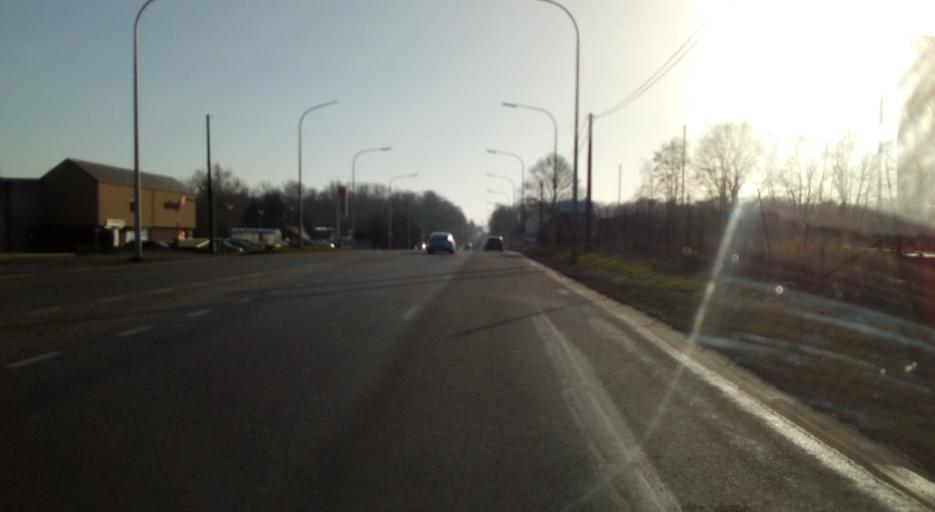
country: BE
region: Wallonia
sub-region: Province du Hainaut
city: Gerpinnes
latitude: 50.3289
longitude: 4.4760
